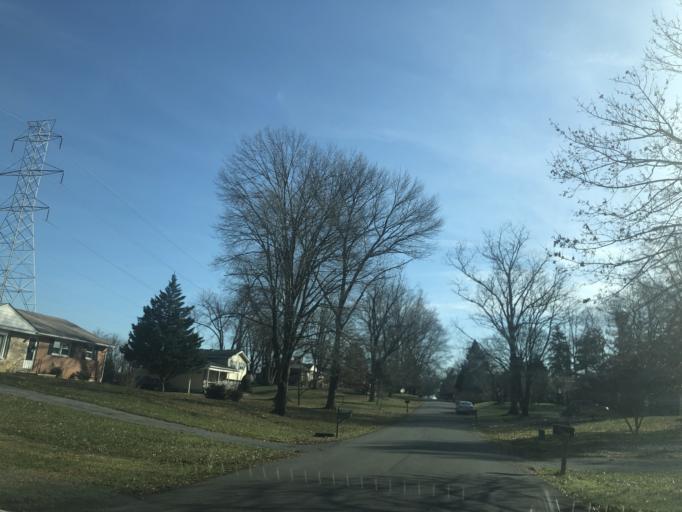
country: US
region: Maryland
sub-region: Howard County
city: Ellicott City
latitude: 39.2895
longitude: -76.8290
